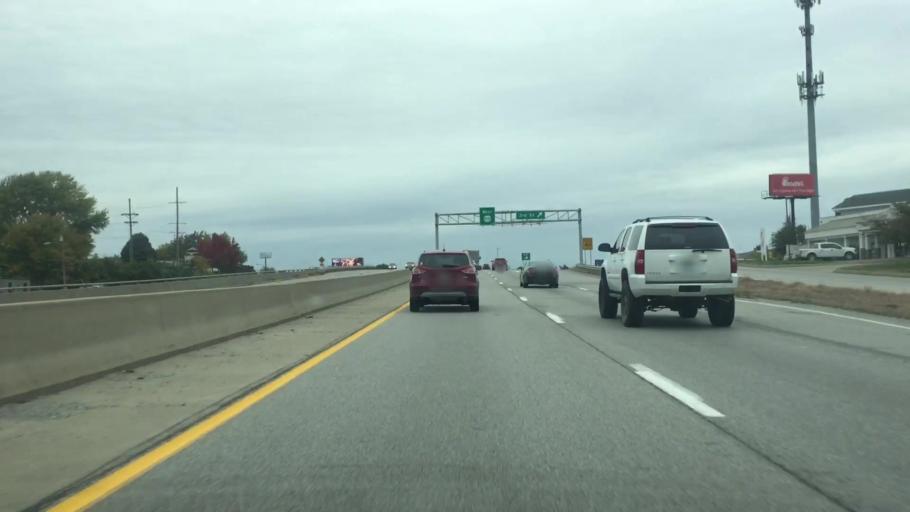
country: US
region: Missouri
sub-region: Jackson County
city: Lees Summit
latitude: 38.9089
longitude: -94.3901
